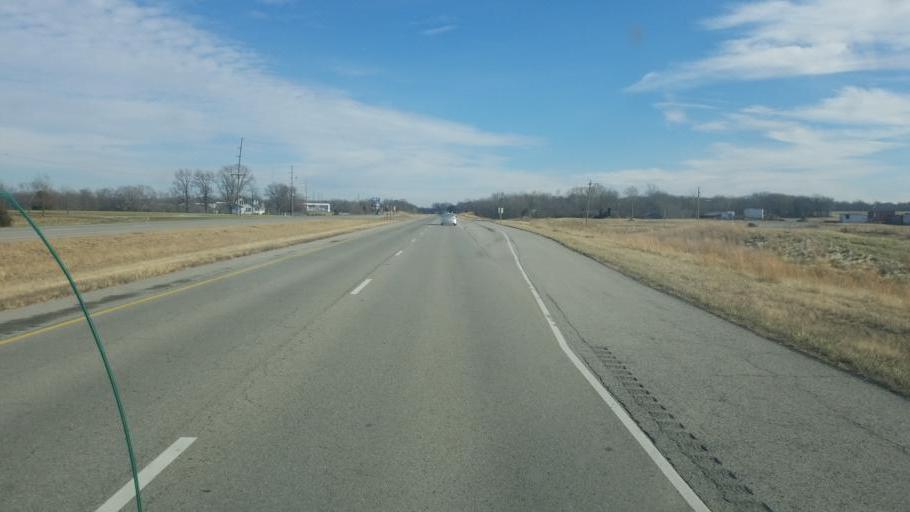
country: US
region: Illinois
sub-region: Williamson County
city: Marion
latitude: 37.7295
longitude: -88.8385
